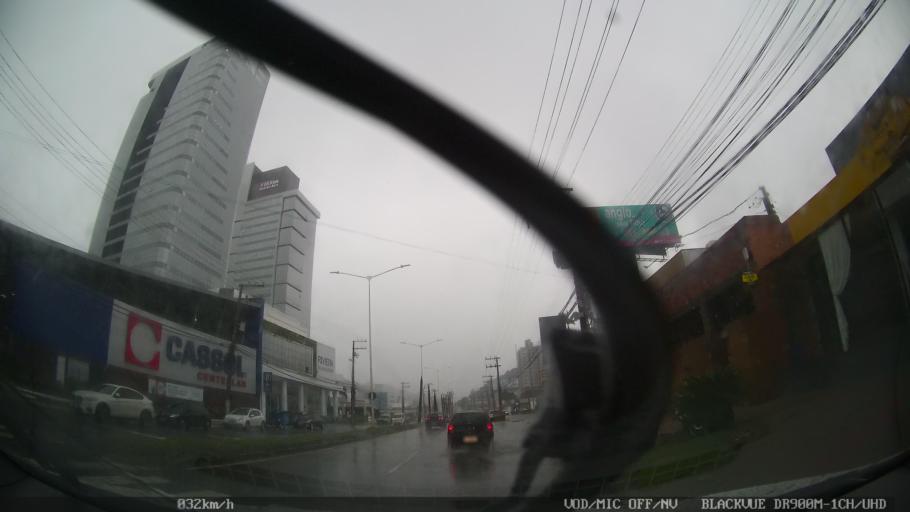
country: BR
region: Santa Catarina
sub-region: Balneario Camboriu
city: Balneario Camboriu
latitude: -26.9524
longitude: -48.6405
